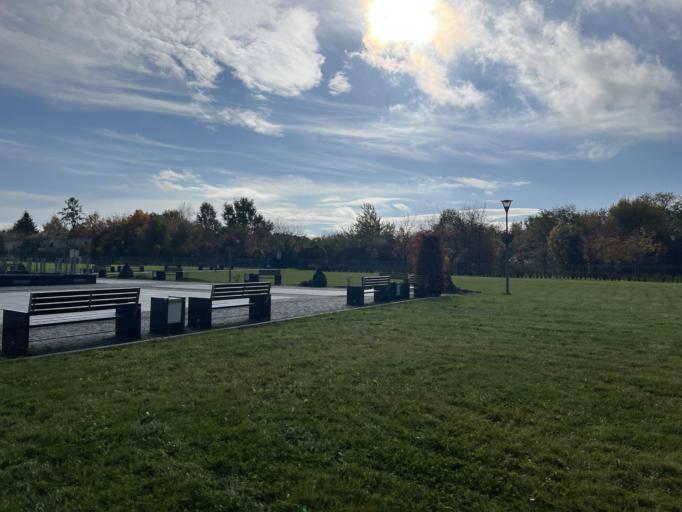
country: PL
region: Silesian Voivodeship
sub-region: Gliwice
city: Gliwice
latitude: 50.3135
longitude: 18.6882
